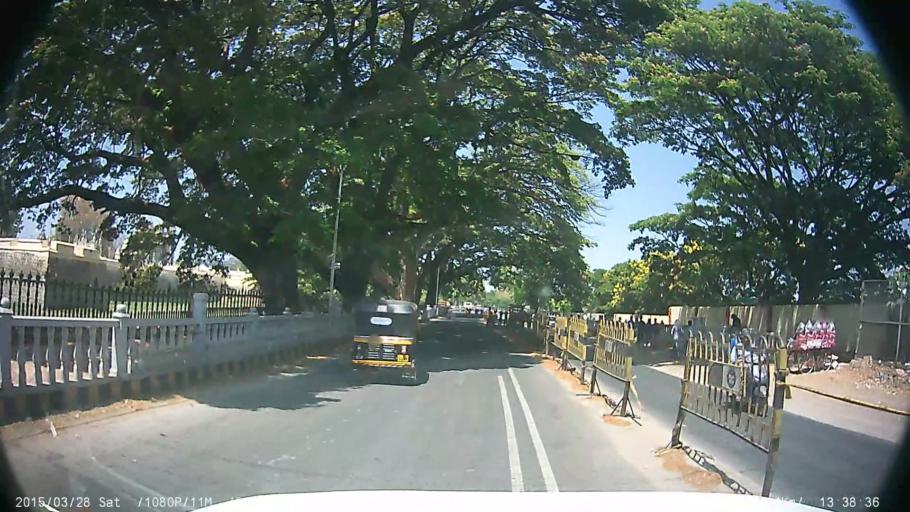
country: IN
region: Karnataka
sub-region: Mysore
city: Mysore
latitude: 12.3029
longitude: 76.6578
